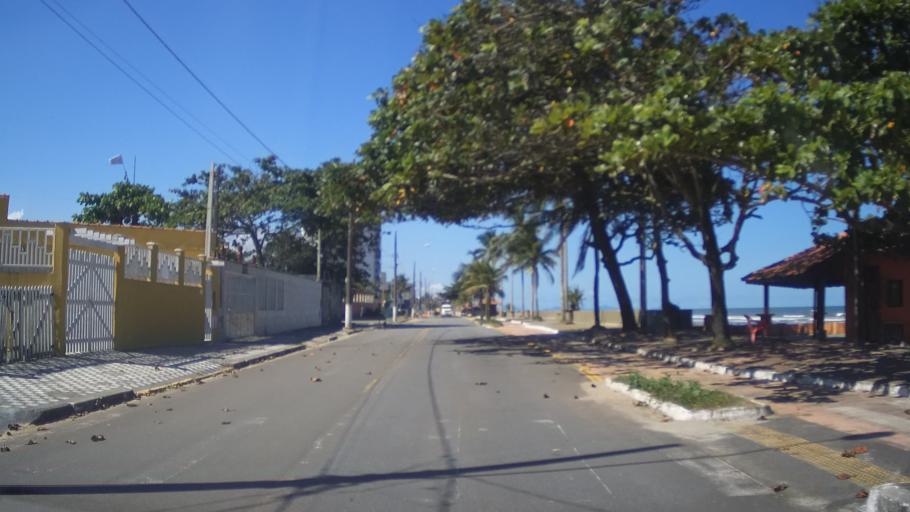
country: BR
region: Sao Paulo
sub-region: Mongagua
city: Mongagua
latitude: -24.1295
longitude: -46.6855
